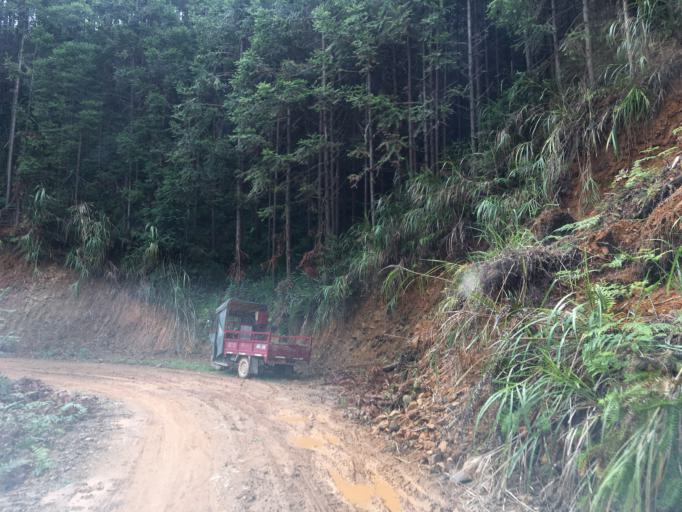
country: CN
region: Guangxi Zhuangzu Zizhiqu
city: Xinzhou
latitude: 24.8679
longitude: 105.8489
